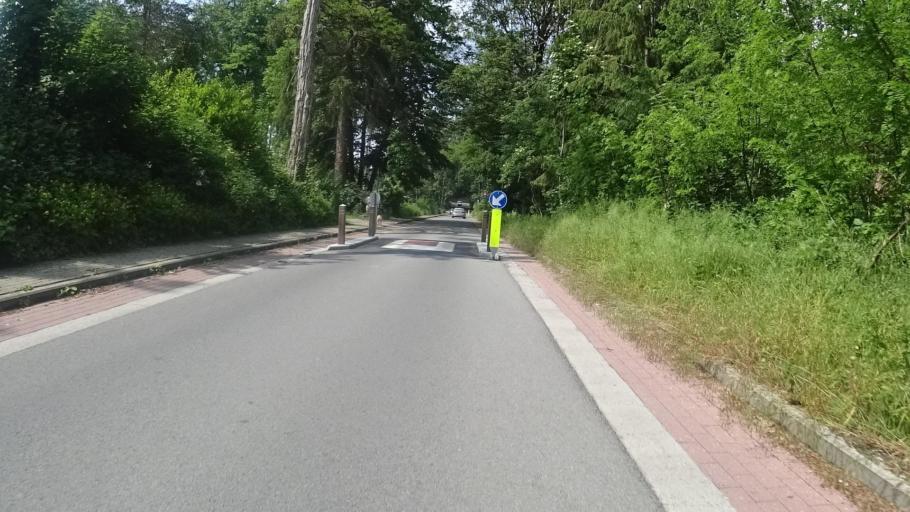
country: BE
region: Wallonia
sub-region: Province du Brabant Wallon
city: Louvain-la-Neuve
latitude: 50.6920
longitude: 4.6308
